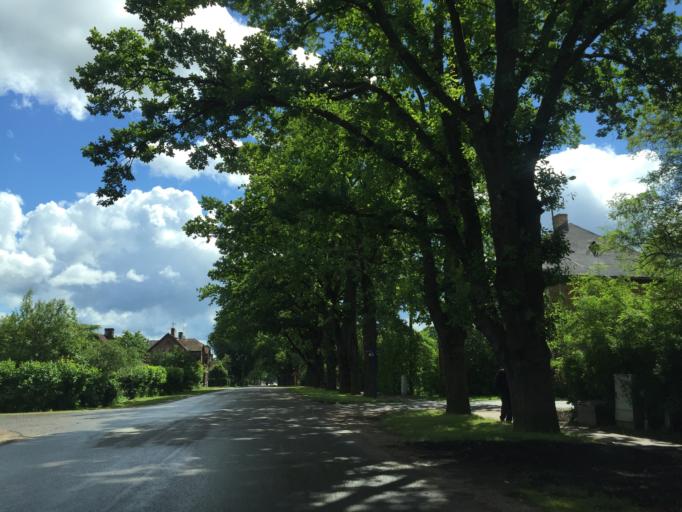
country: LV
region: Lecava
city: Iecava
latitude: 56.5966
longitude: 24.2000
